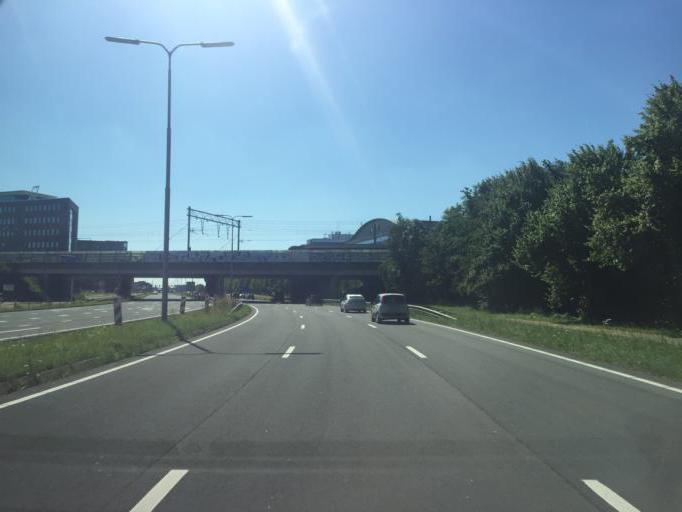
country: NL
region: North Holland
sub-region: Gemeente Haarlemmermeer
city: Hoofddorp
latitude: 52.2965
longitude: 4.7096
